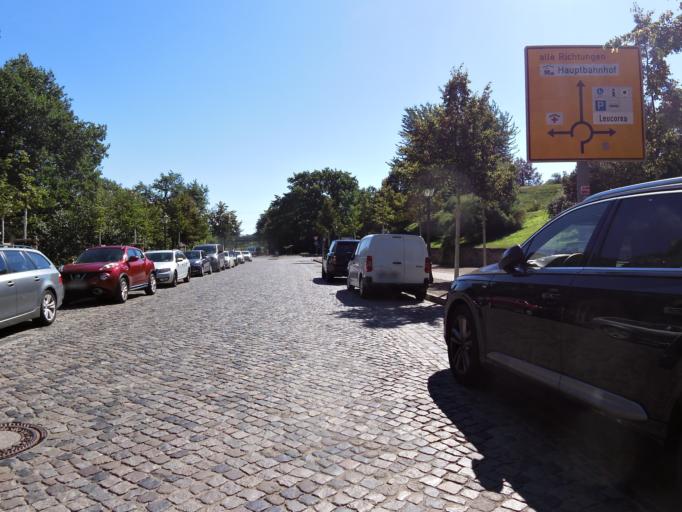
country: DE
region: Saxony-Anhalt
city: Wittenburg
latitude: 51.8643
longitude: 12.6541
